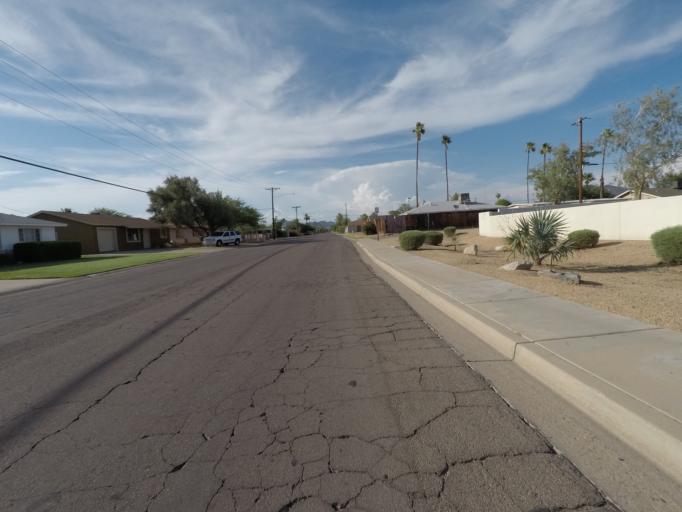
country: US
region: Arizona
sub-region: Maricopa County
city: Phoenix
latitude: 33.4673
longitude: -112.0085
